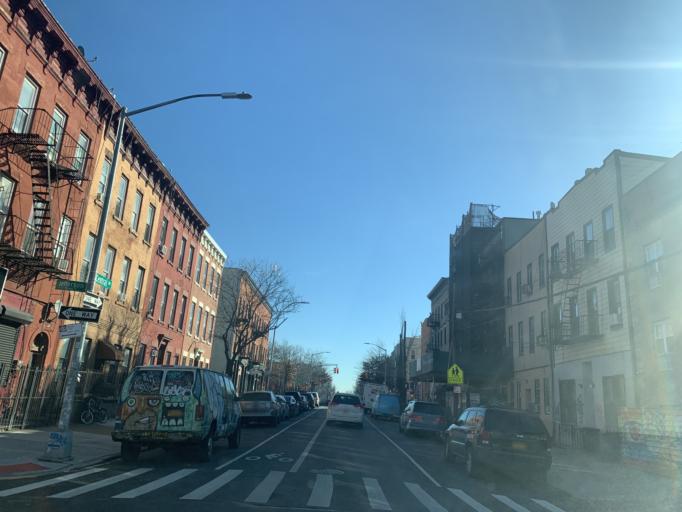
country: US
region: New York
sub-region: Queens County
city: Long Island City
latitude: 40.7008
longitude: -73.9299
